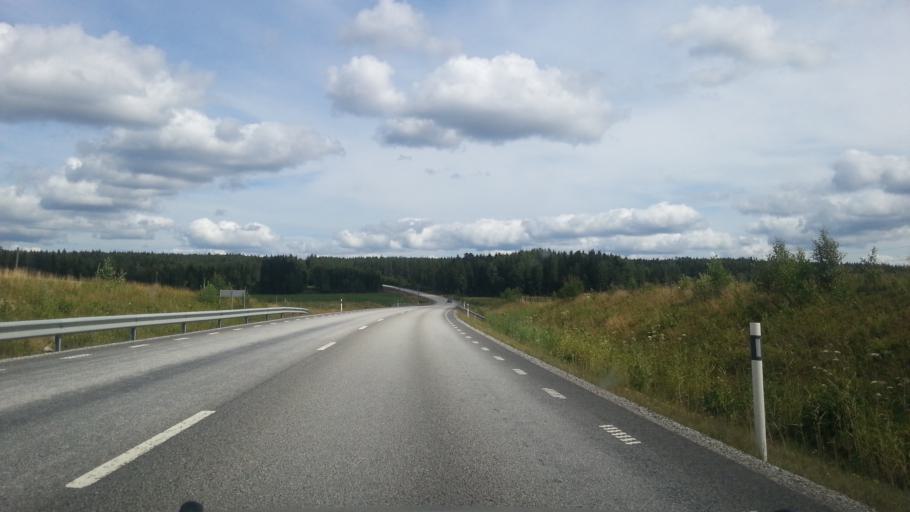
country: SE
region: OErebro
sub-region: Lindesbergs Kommun
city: Lindesberg
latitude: 59.7512
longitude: 15.4408
